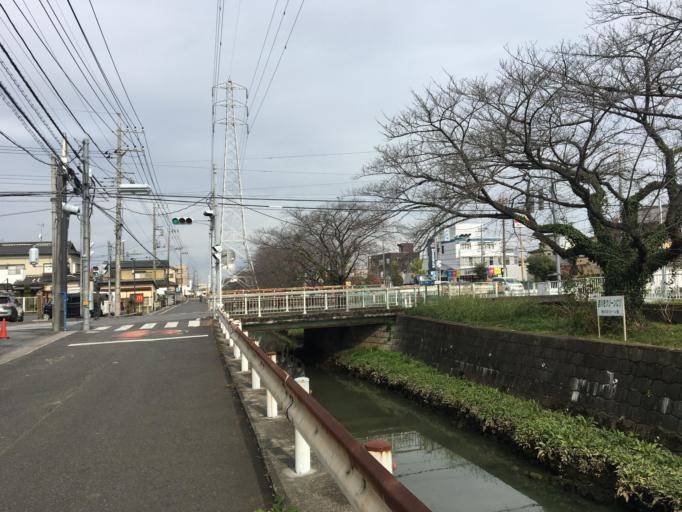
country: JP
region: Saitama
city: Yoshikawa
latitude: 35.8849
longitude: 139.8462
